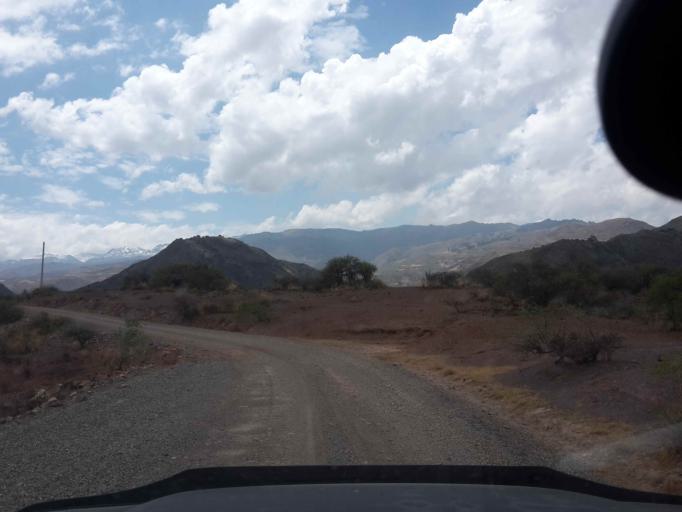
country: BO
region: Cochabamba
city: Sipe Sipe
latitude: -17.5383
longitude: -66.4853
